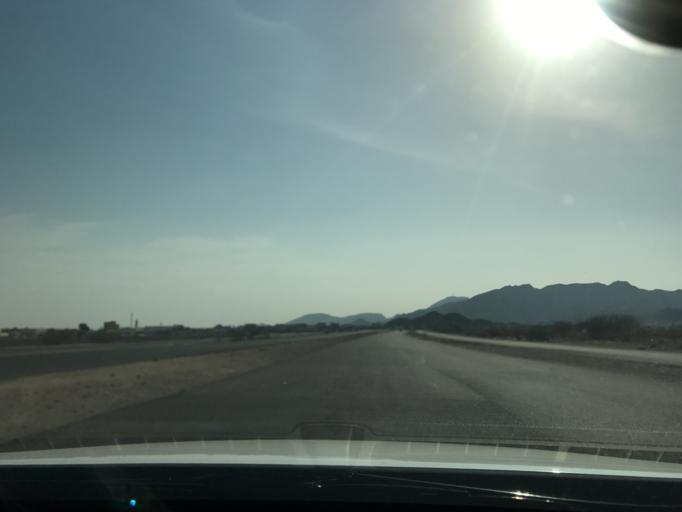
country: SA
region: Makkah
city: Al Jumum
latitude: 21.4526
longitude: 39.5299
